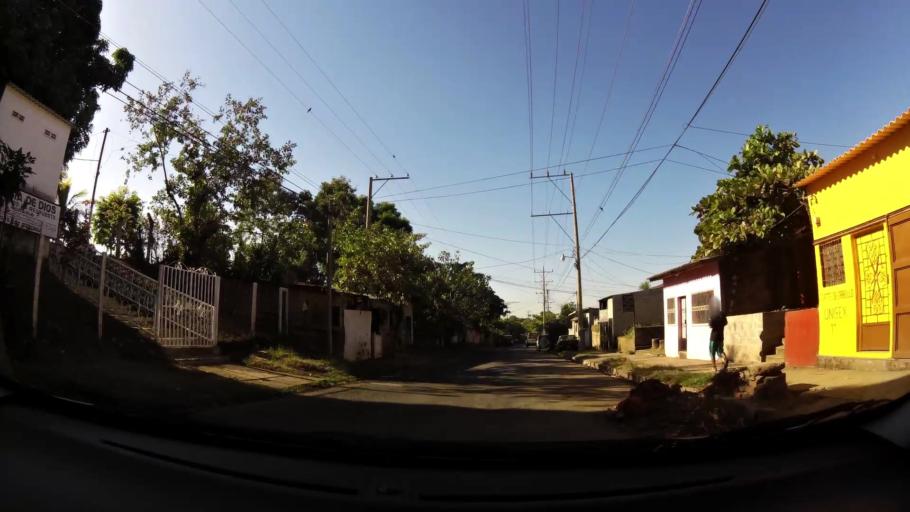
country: SV
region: Sonsonate
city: Sonzacate
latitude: 13.7411
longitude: -89.7127
